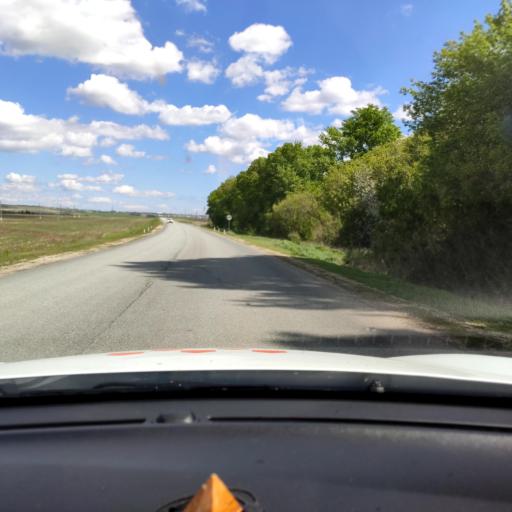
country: RU
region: Tatarstan
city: Kuybyshevskiy Zaton
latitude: 55.1614
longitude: 49.1962
